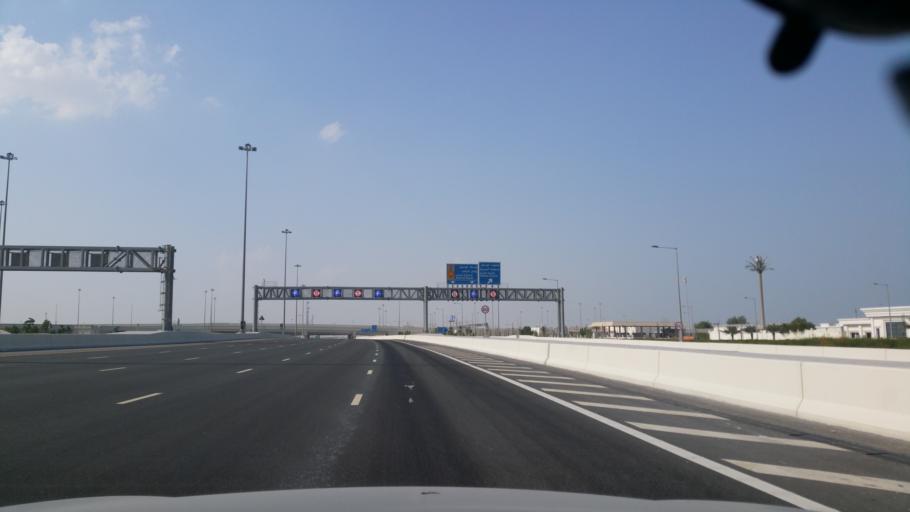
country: QA
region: Baladiyat Umm Salal
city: Umm Salal Muhammad
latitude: 25.3887
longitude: 51.4996
